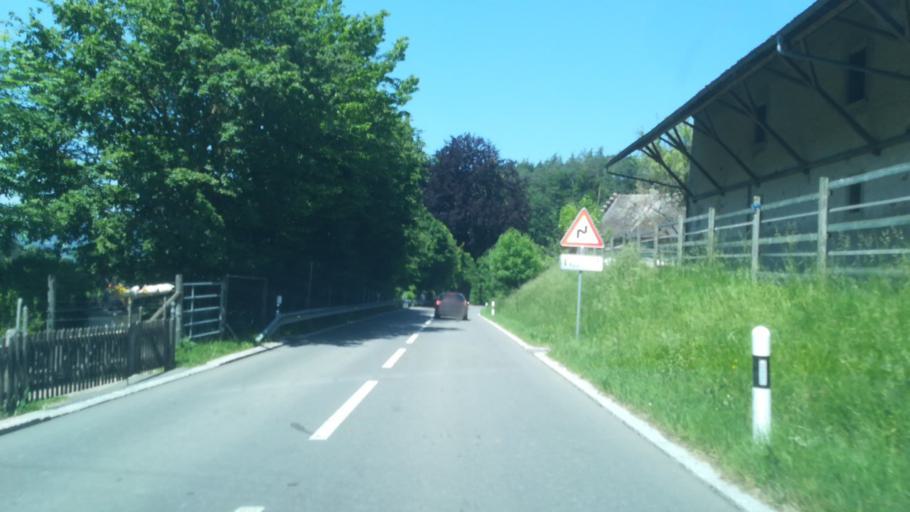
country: CH
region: Thurgau
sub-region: Frauenfeld District
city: Pfyn
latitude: 47.6301
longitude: 8.9260
